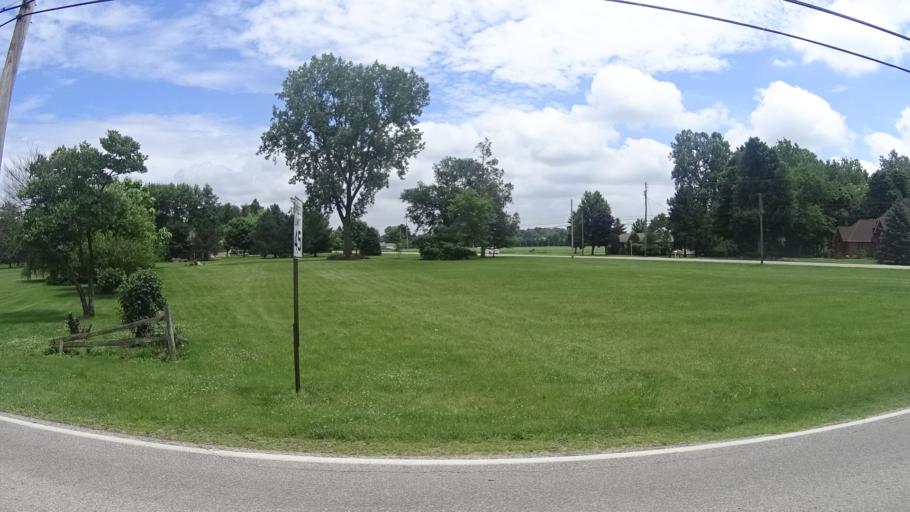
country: US
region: Ohio
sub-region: Erie County
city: Milan
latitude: 41.2994
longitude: -82.5895
